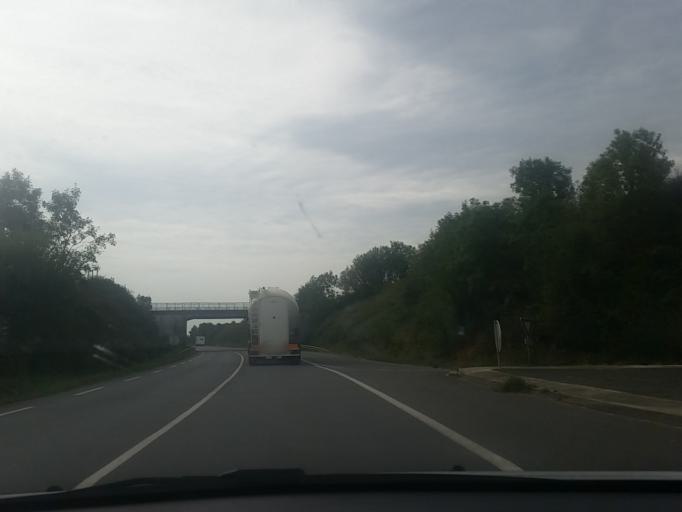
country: FR
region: Pays de la Loire
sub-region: Departement de la Vendee
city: Chantonnay
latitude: 46.6837
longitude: -1.0664
